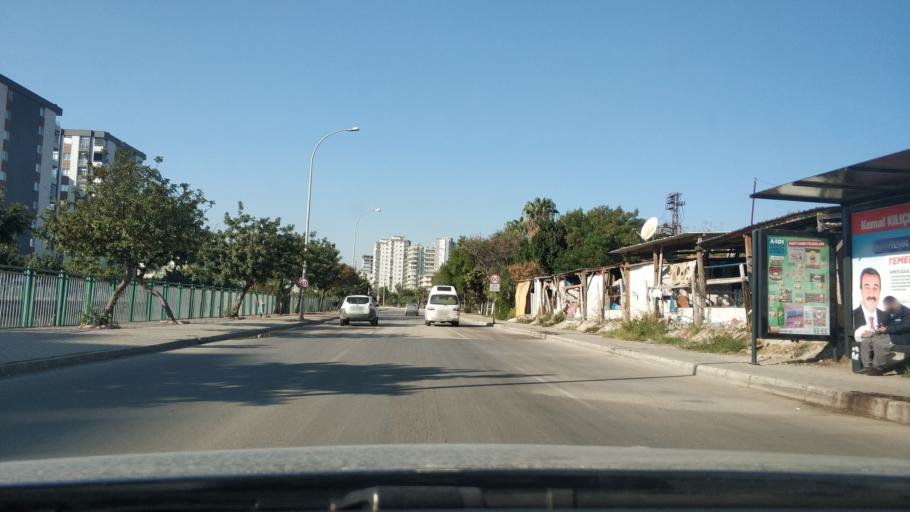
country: TR
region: Adana
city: Seyhan
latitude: 37.0111
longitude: 35.2969
